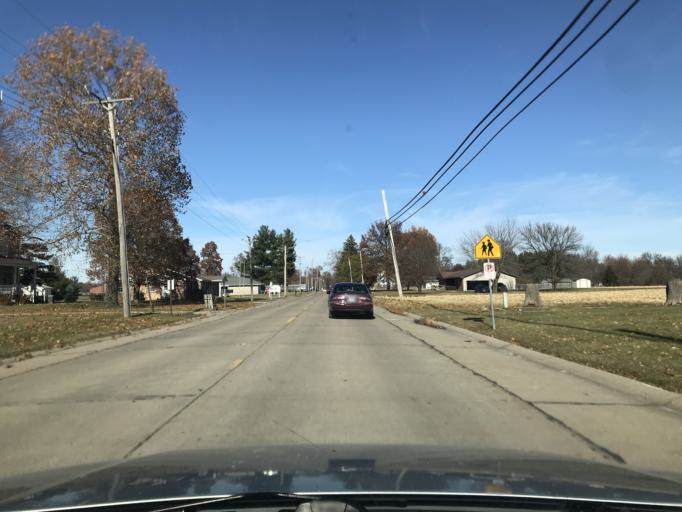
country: US
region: Illinois
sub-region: McDonough County
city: Macomb
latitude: 40.4414
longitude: -90.6709
